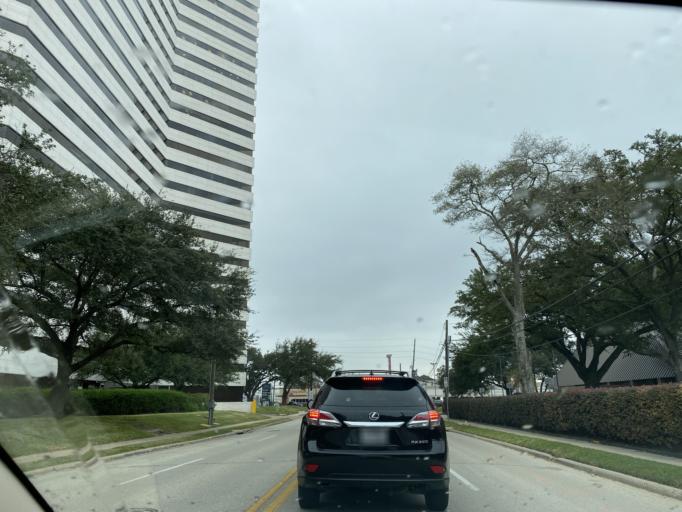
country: US
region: Texas
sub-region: Harris County
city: Hunters Creek Village
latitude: 29.7391
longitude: -95.4794
